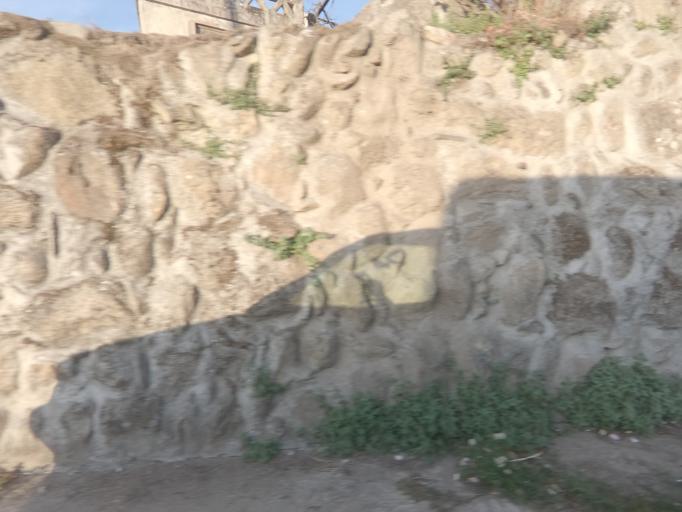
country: PT
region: Vila Real
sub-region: Vila Real
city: Vila Real
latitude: 41.3158
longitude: -7.7660
